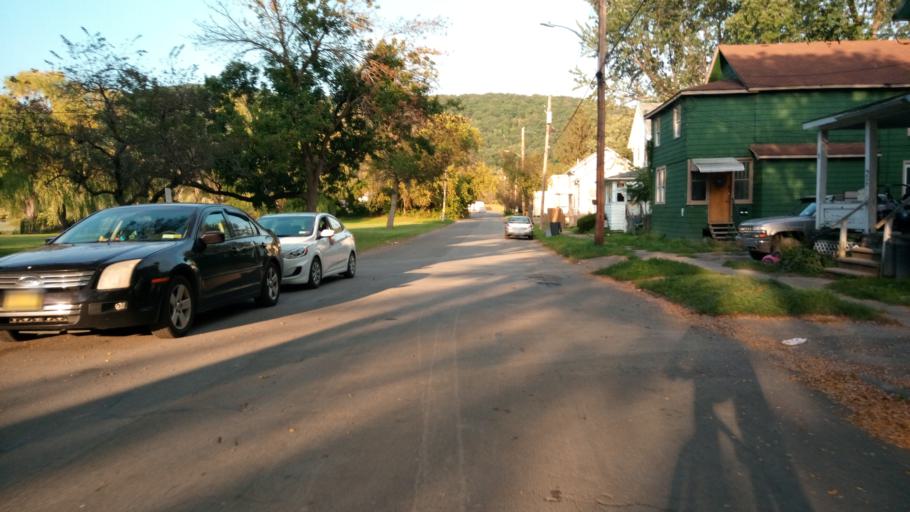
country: US
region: New York
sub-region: Chemung County
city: Elmira
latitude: 42.1053
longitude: -76.8033
